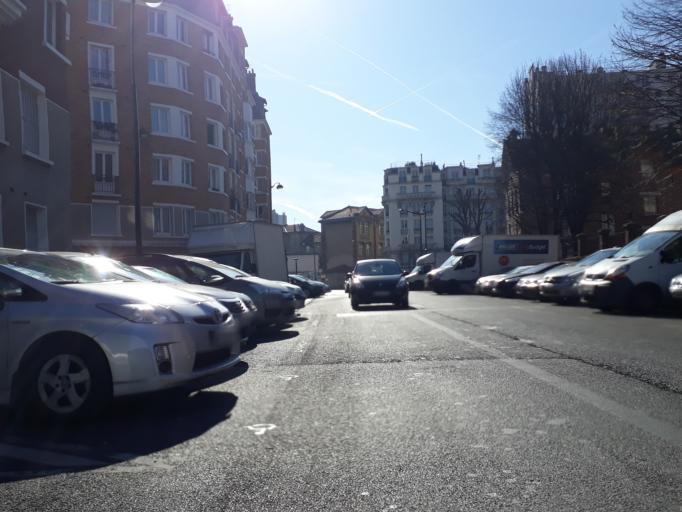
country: FR
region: Ile-de-France
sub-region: Paris
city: Saint-Ouen
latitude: 48.8983
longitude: 2.3241
